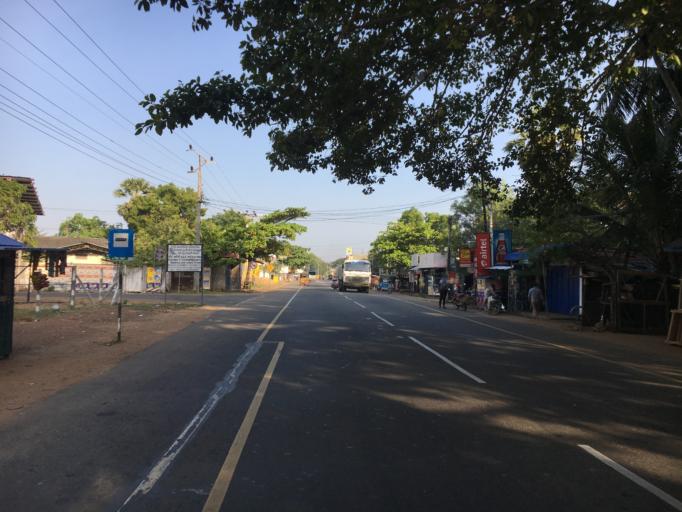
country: LK
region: Eastern Province
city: Eravur Town
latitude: 7.9090
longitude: 81.5324
